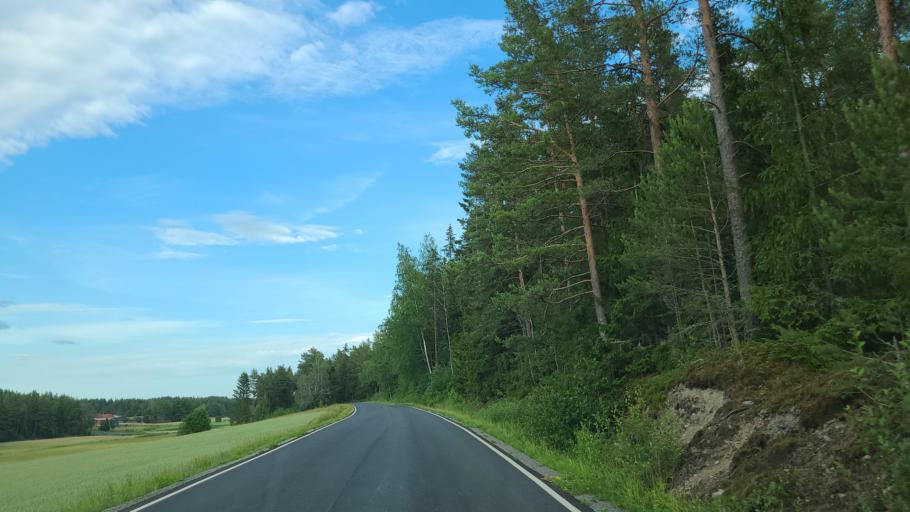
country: FI
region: Varsinais-Suomi
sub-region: Turku
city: Rymaettylae
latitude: 60.3256
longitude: 21.9626
